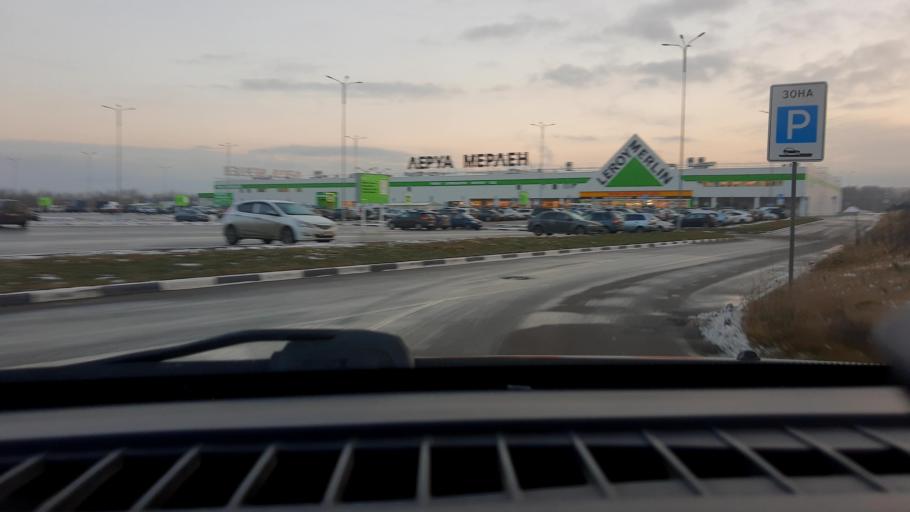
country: RU
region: Nizjnij Novgorod
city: Gorbatovka
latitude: 56.3090
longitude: 43.7699
